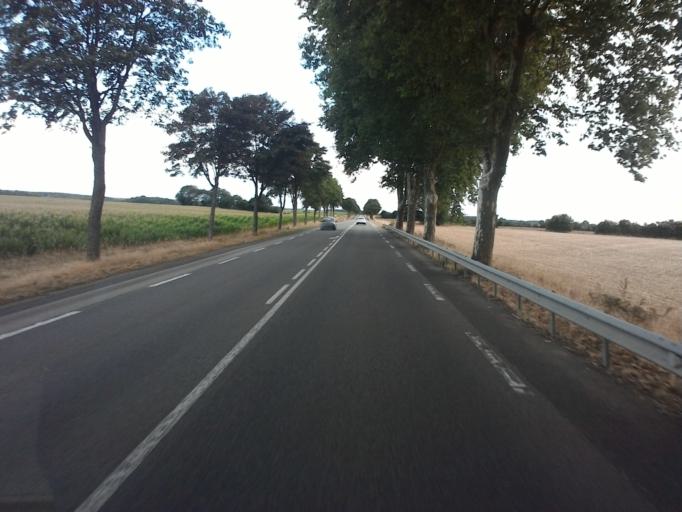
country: FR
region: Rhone-Alpes
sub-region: Departement de l'Ain
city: Saint-Martin-du-Mont
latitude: 46.1027
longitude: 5.3080
